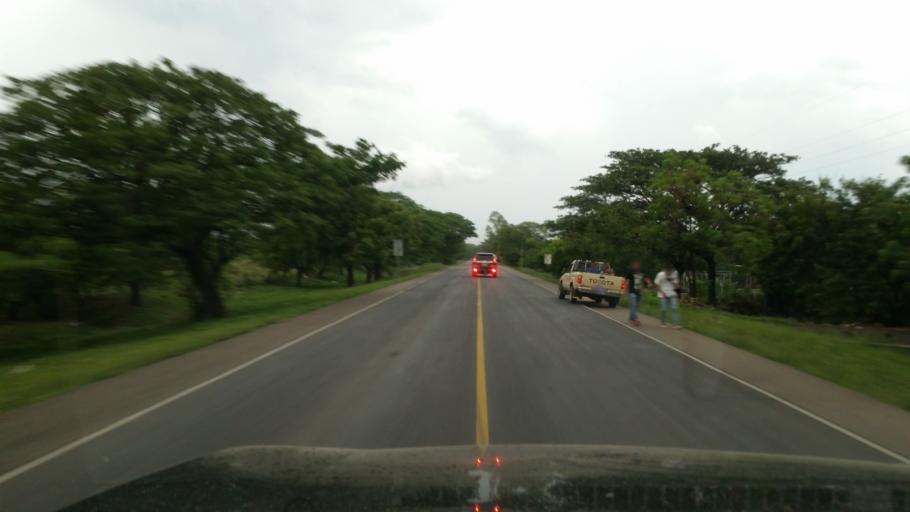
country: NI
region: Chinandega
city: Puerto Morazan
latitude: 12.7719
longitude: -87.0557
